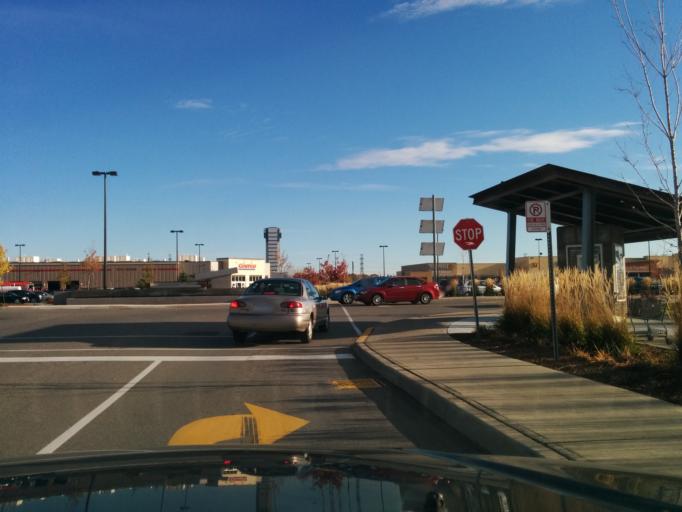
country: CA
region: Ontario
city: Etobicoke
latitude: 43.6113
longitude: -79.5783
